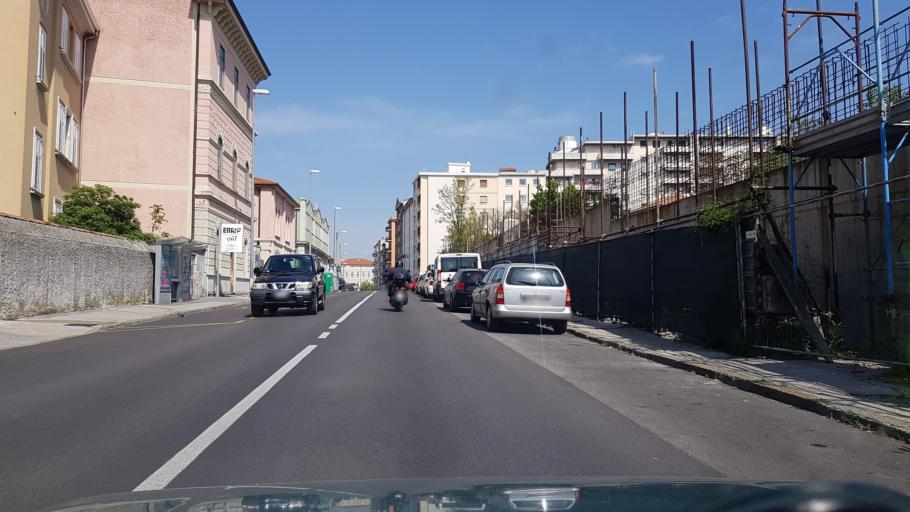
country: IT
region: Friuli Venezia Giulia
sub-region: Provincia di Trieste
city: Trieste
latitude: 45.6369
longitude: 13.7855
